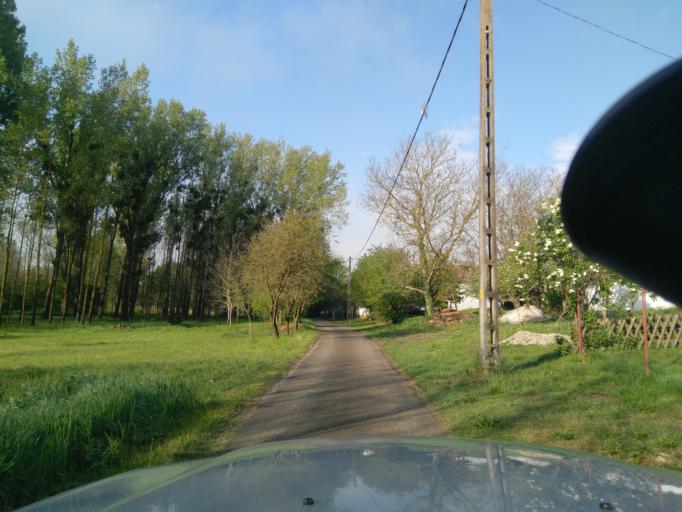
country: HU
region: Zala
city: Sarmellek
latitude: 46.7403
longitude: 17.1399
